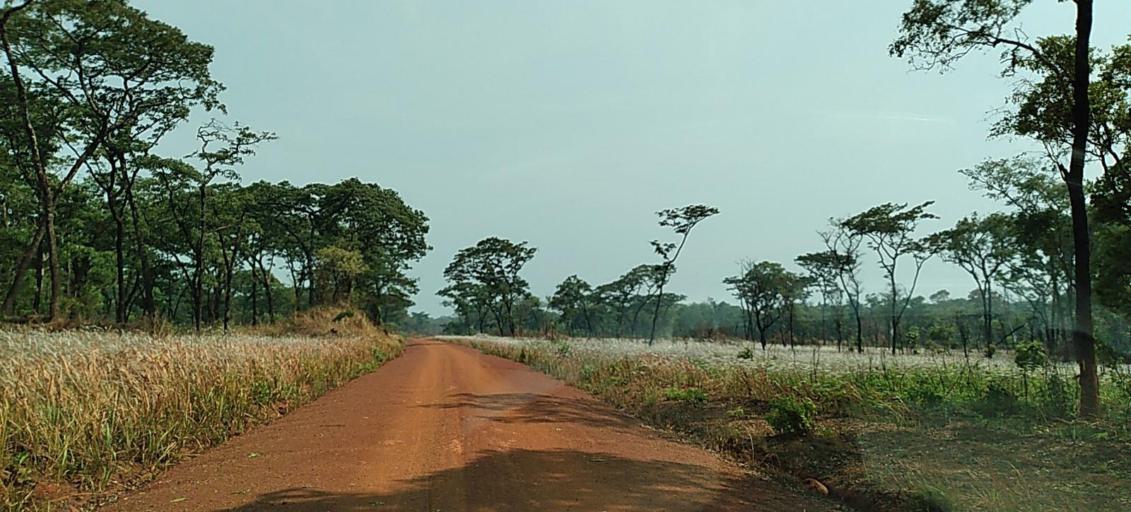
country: ZM
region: North-Western
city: Kansanshi
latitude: -12.0243
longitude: 26.8513
